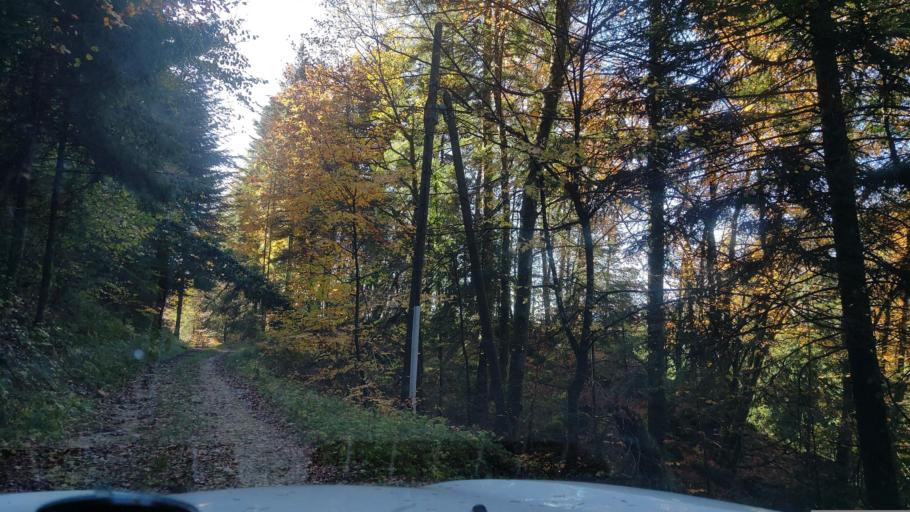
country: FR
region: Rhone-Alpes
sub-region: Departement de la Savoie
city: Les Echelles
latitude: 45.4645
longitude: 5.8228
